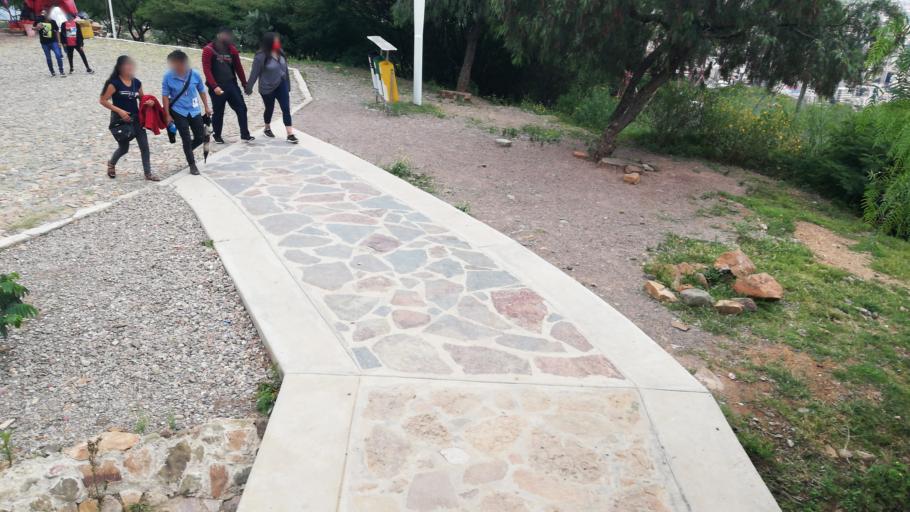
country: BO
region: Cochabamba
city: Cochabamba
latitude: -17.3844
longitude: -66.1356
